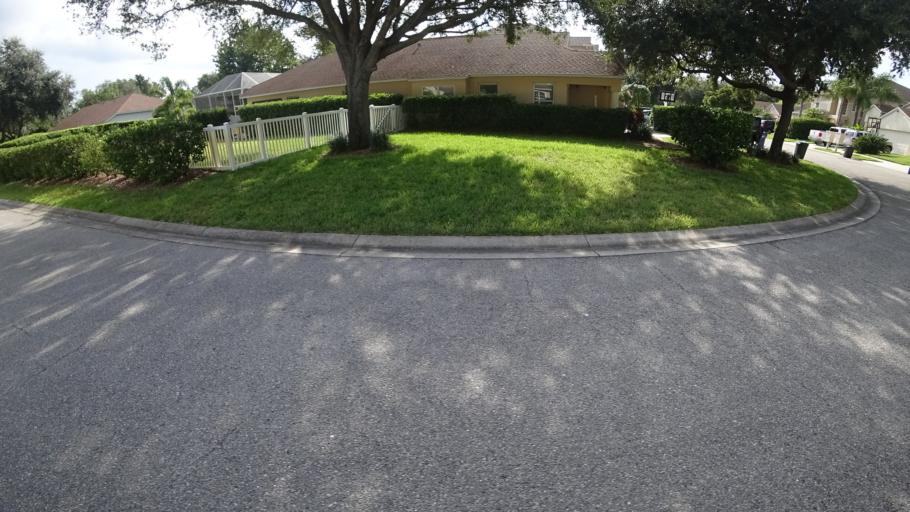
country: US
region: Florida
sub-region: Sarasota County
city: The Meadows
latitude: 27.4293
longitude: -82.4309
